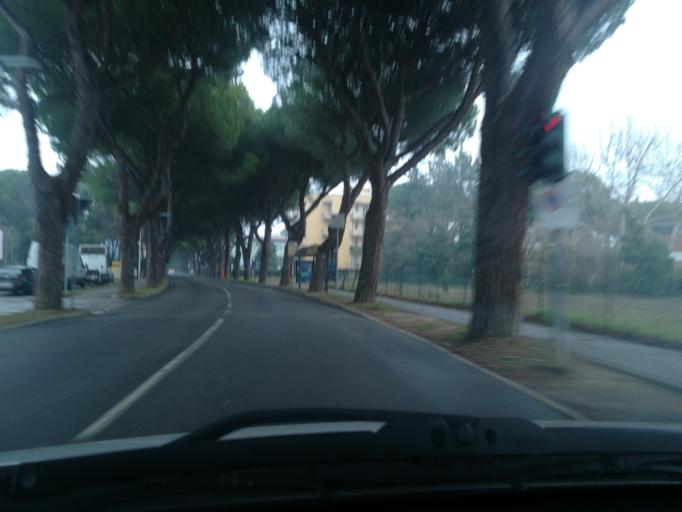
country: IT
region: Emilia-Romagna
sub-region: Provincia di Rimini
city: Riccione
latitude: 44.0029
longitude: 12.6443
